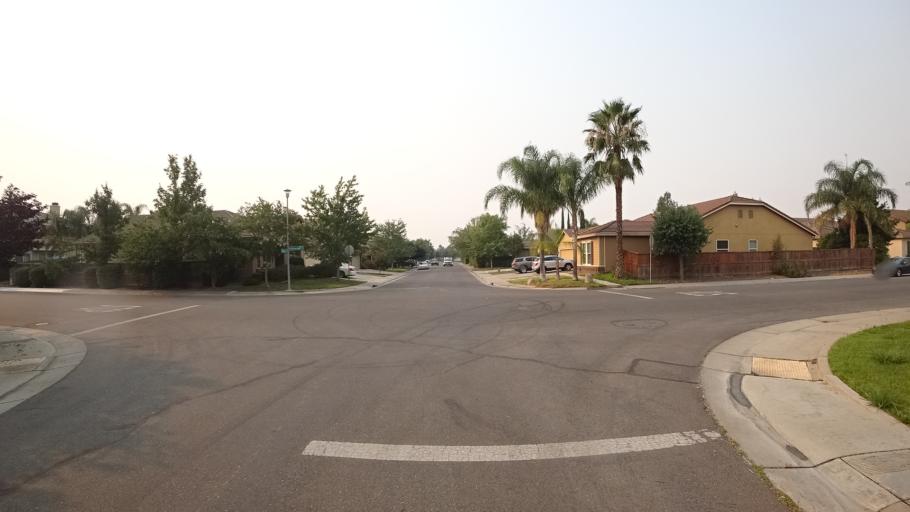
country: US
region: California
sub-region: Sacramento County
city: Laguna
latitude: 38.3995
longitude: -121.4457
